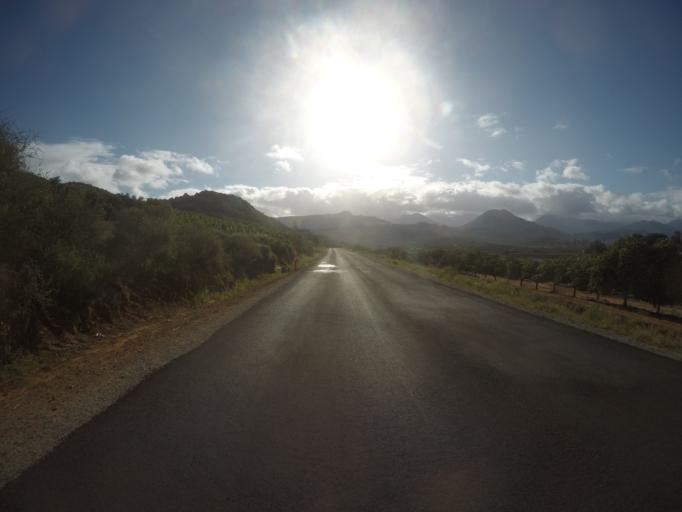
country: ZA
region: Western Cape
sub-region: West Coast District Municipality
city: Clanwilliam
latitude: -32.4309
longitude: 18.9513
